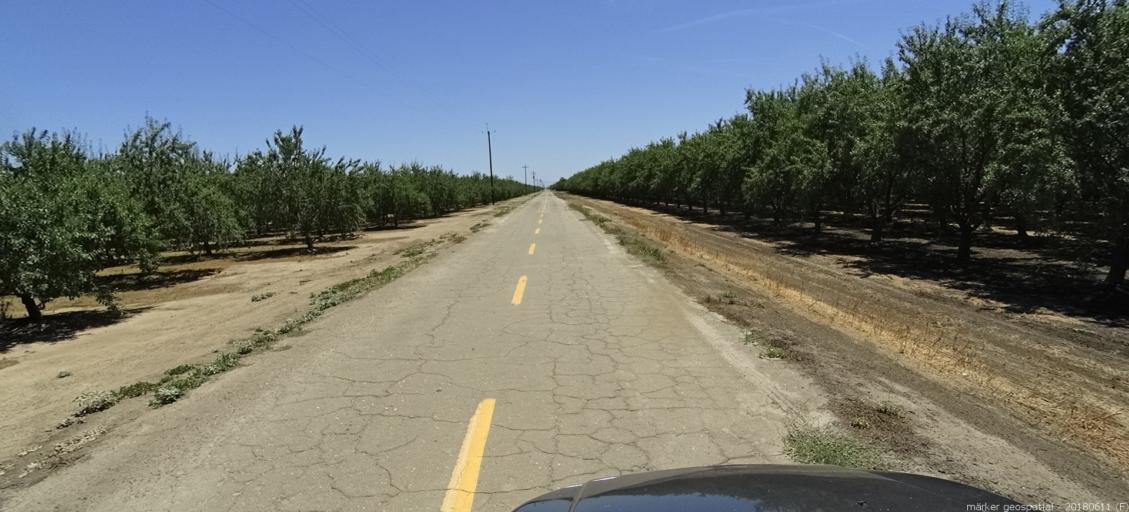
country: US
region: California
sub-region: Madera County
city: Fairmead
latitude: 37.0546
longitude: -120.2101
